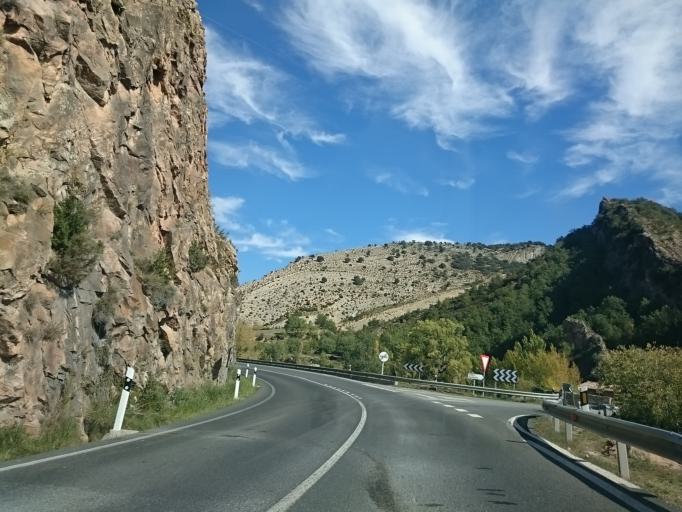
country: ES
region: Aragon
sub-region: Provincia de Huesca
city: Areny de Noguera / Aren
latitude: 42.2553
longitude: 0.7350
